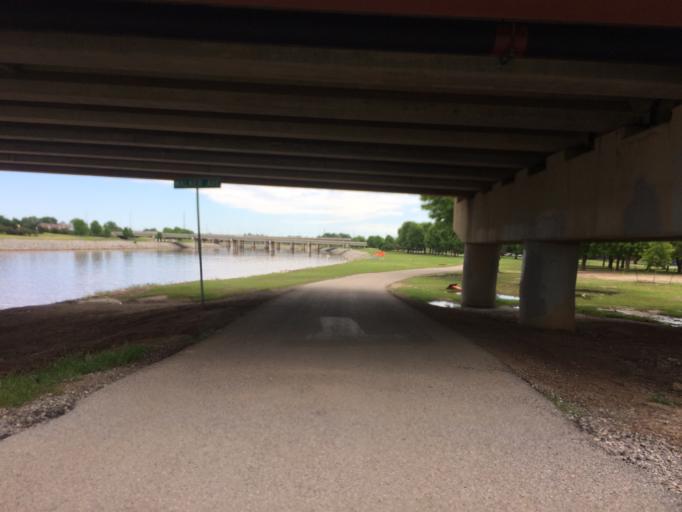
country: US
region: Oklahoma
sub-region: Oklahoma County
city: Oklahoma City
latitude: 35.4476
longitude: -97.5214
